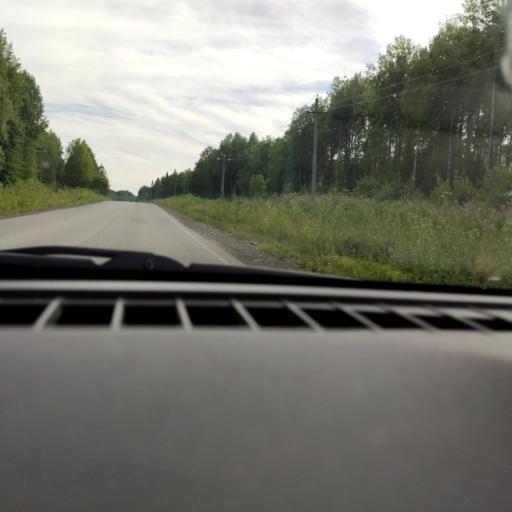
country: RU
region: Perm
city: Polazna
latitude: 58.3210
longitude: 56.1491
